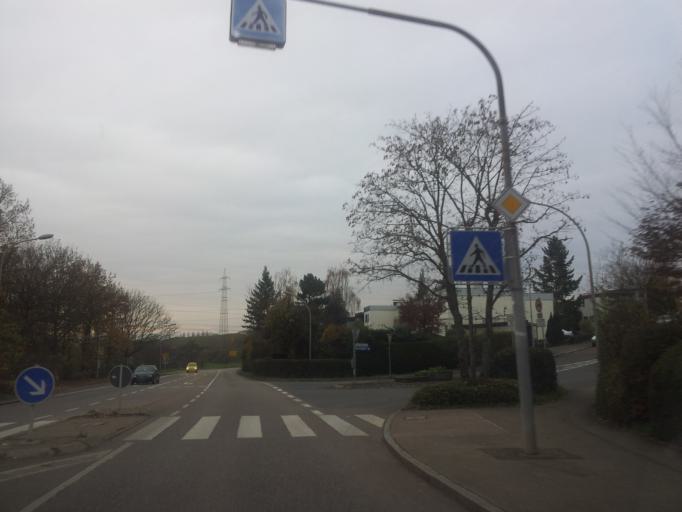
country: DE
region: Baden-Wuerttemberg
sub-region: Regierungsbezirk Stuttgart
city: Korb
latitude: 48.8406
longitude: 9.3525
